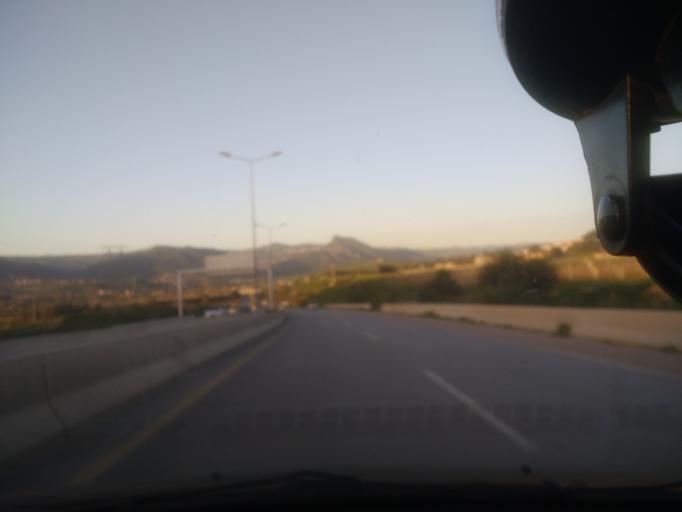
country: DZ
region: Boumerdes
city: Draa Ben Khedda
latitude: 36.7395
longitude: 4.0068
